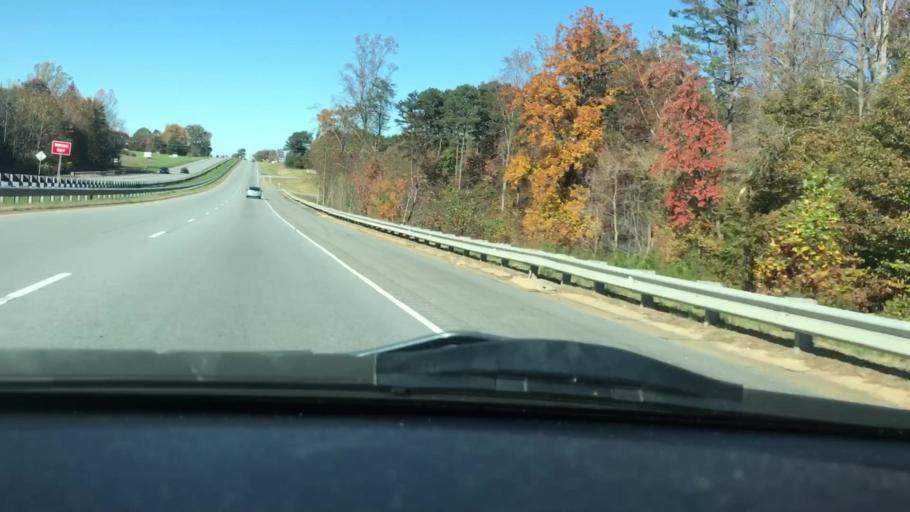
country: US
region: North Carolina
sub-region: Guilford County
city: Stokesdale
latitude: 36.3023
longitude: -79.9409
